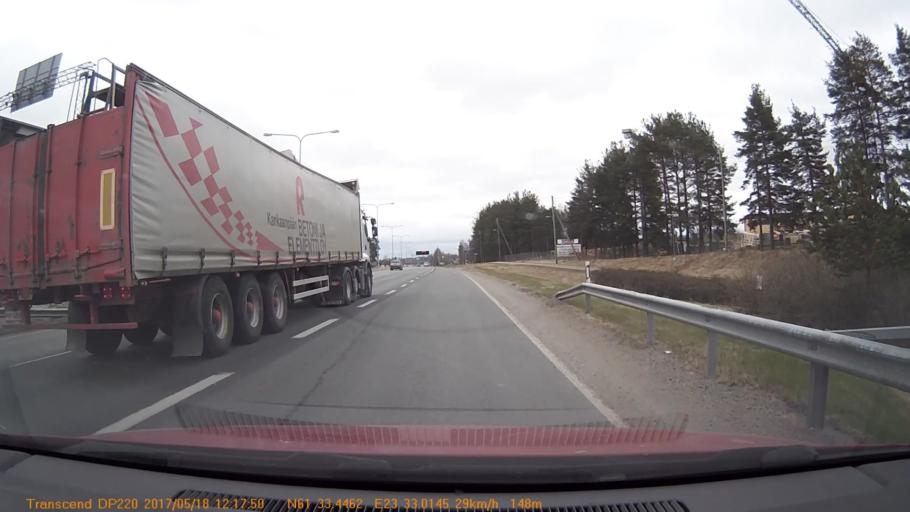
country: FI
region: Pirkanmaa
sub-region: Tampere
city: Yloejaervi
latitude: 61.5574
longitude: 23.5503
